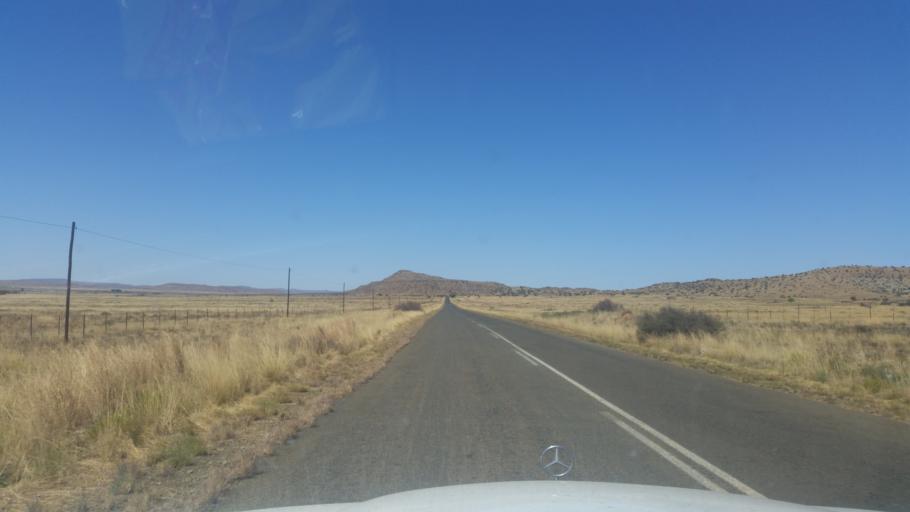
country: ZA
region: Eastern Cape
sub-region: Joe Gqabi District Municipality
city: Burgersdorp
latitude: -30.7204
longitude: 25.7552
